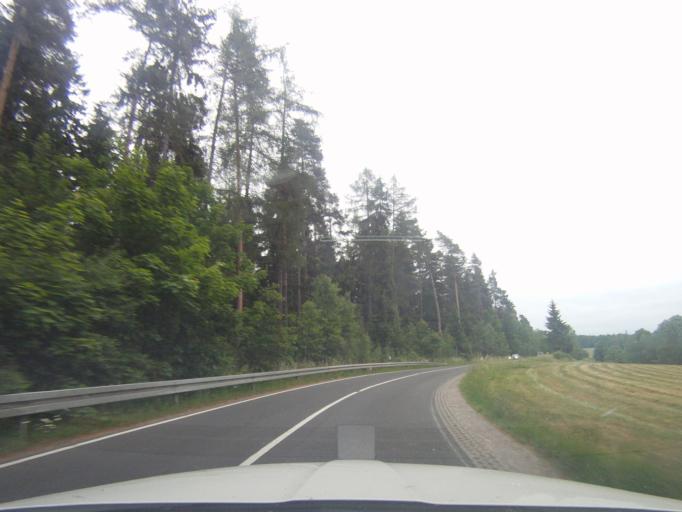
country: DE
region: Thuringia
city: Sankt Kilian
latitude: 50.4939
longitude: 10.8287
